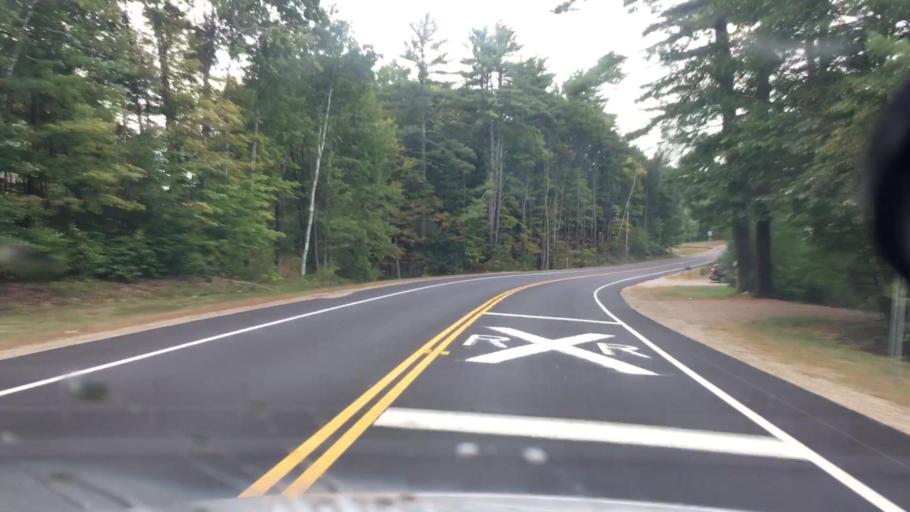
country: US
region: New Hampshire
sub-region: Carroll County
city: Sanbornville
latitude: 43.5240
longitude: -71.0257
